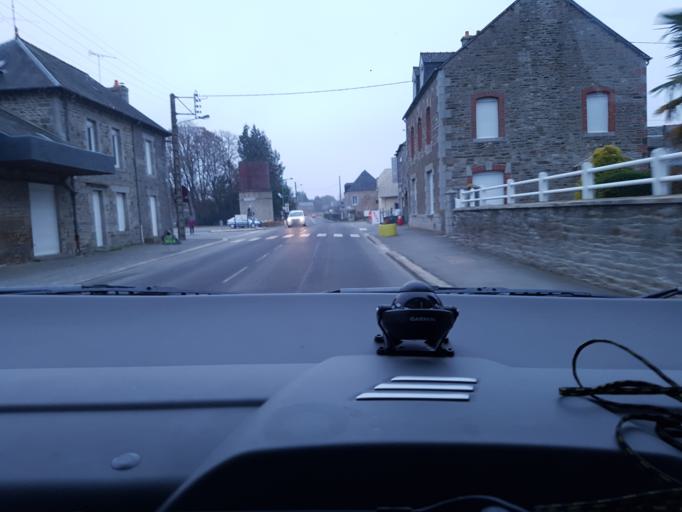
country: FR
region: Brittany
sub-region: Departement d'Ille-et-Vilaine
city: Saint-Brice-en-Cogles
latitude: 48.4076
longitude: -1.3684
